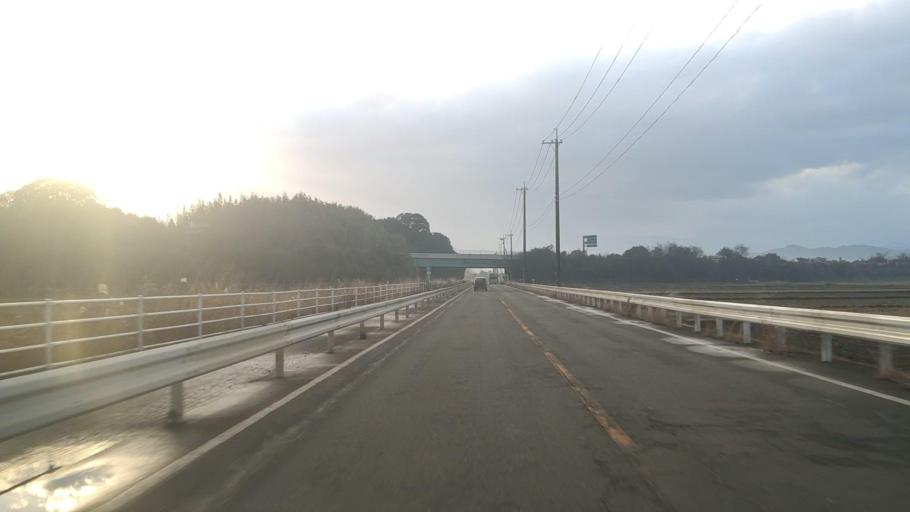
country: JP
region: Kumamoto
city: Uto
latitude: 32.7222
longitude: 130.7688
